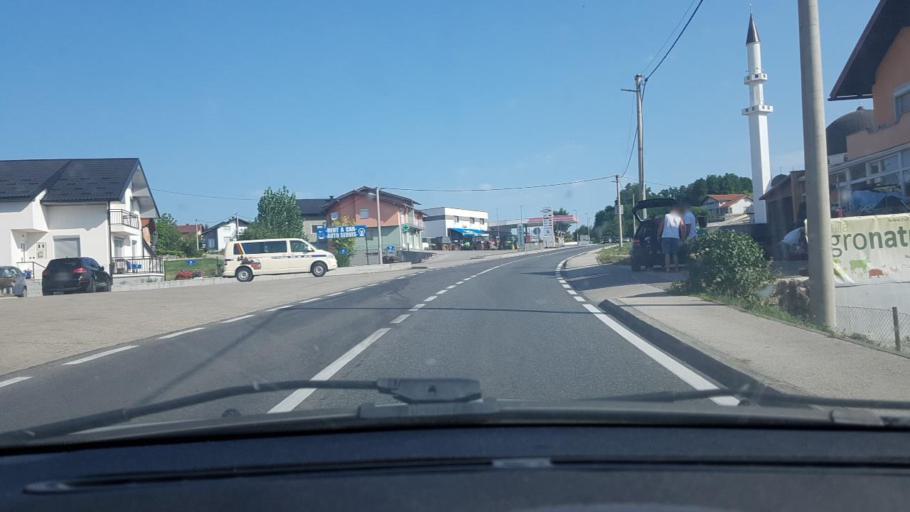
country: BA
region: Federation of Bosnia and Herzegovina
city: Ostrozac
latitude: 44.9096
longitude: 15.9315
